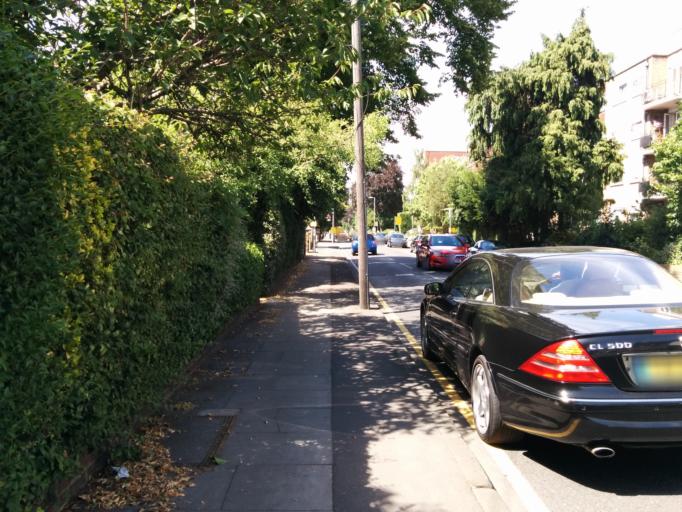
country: GB
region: England
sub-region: Greater London
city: Kingston upon Thames
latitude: 51.4166
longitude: -0.2846
